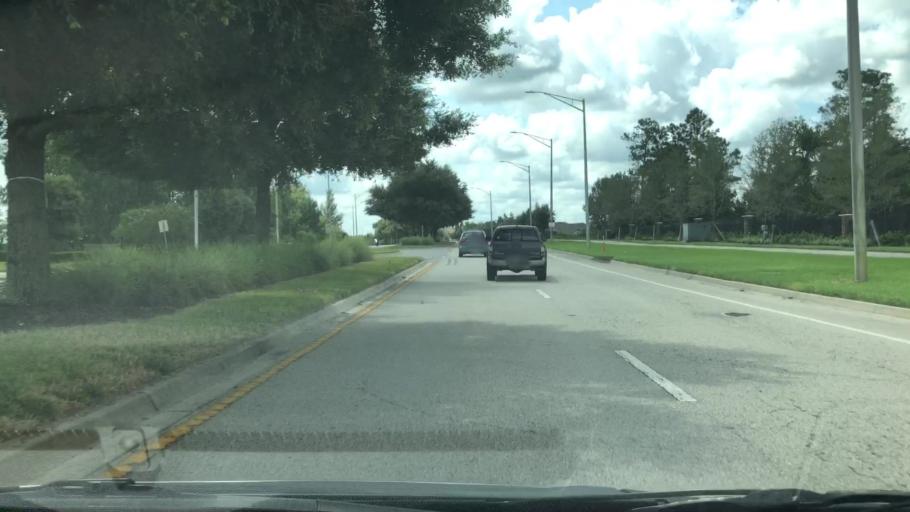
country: US
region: Florida
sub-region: Saint Johns County
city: Fruit Cove
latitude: 30.1185
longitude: -81.5223
